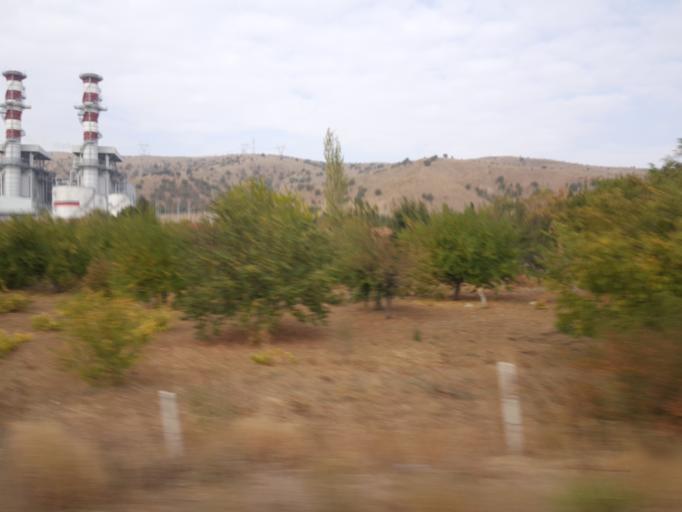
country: TR
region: Kirikkale
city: Bahsili
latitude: 39.7571
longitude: 33.4554
